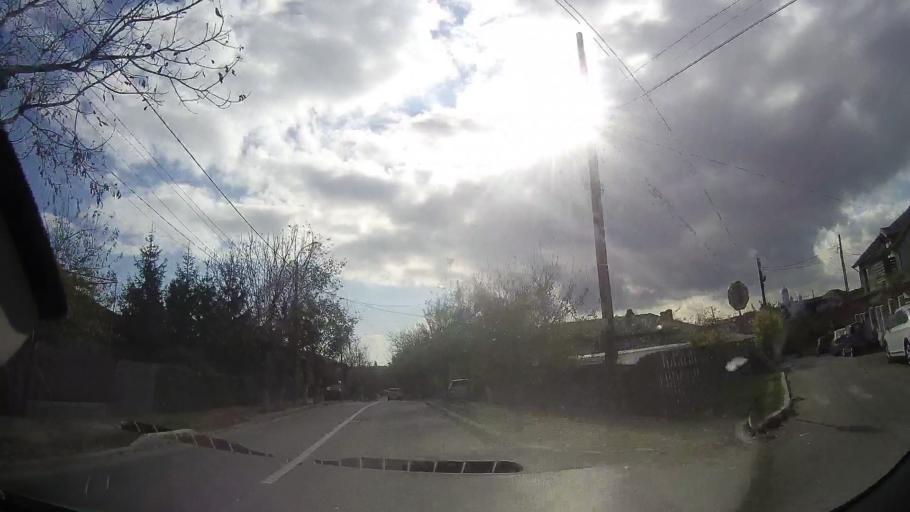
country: RO
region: Constanta
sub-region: Oras Techirghiol
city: Techirghiol
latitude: 44.0578
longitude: 28.5999
